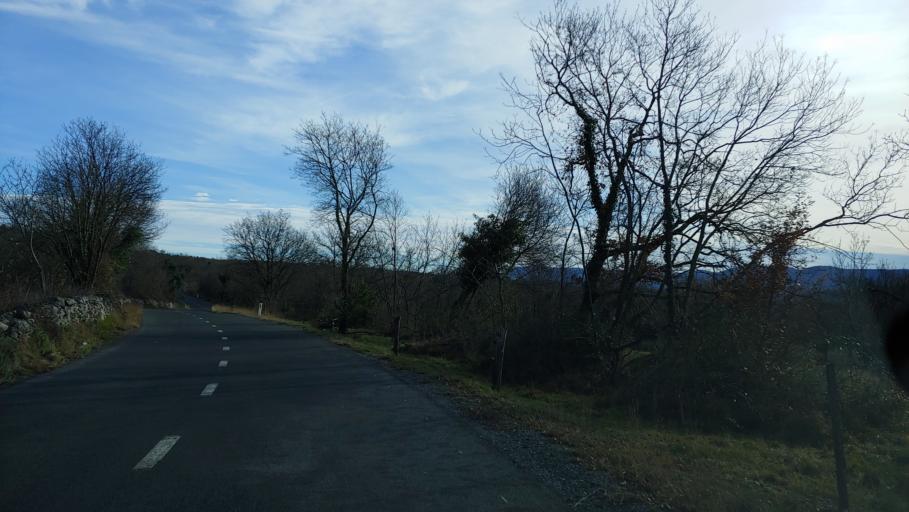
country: IT
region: Friuli Venezia Giulia
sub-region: Provincia di Trieste
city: Sistiana-Visogliano
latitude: 45.8118
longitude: 13.6771
